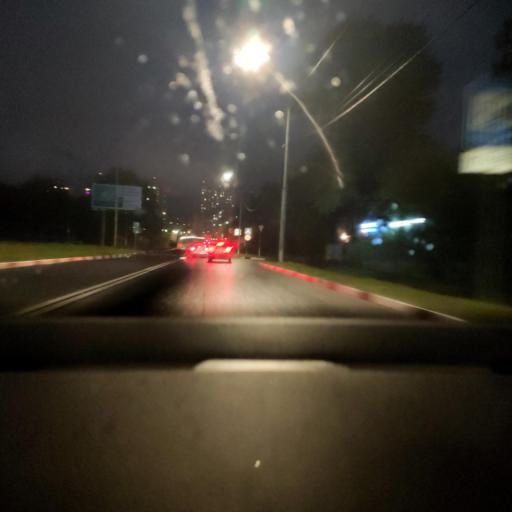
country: RU
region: Moskovskaya
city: Balashikha
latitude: 55.8313
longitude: 37.9495
